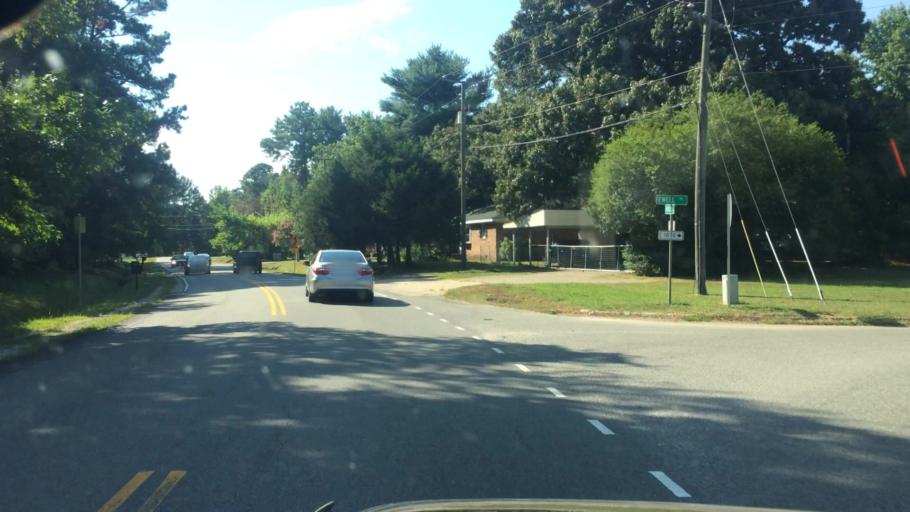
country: US
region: Virginia
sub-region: James City County
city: Williamsburg
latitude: 37.3167
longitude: -76.7317
